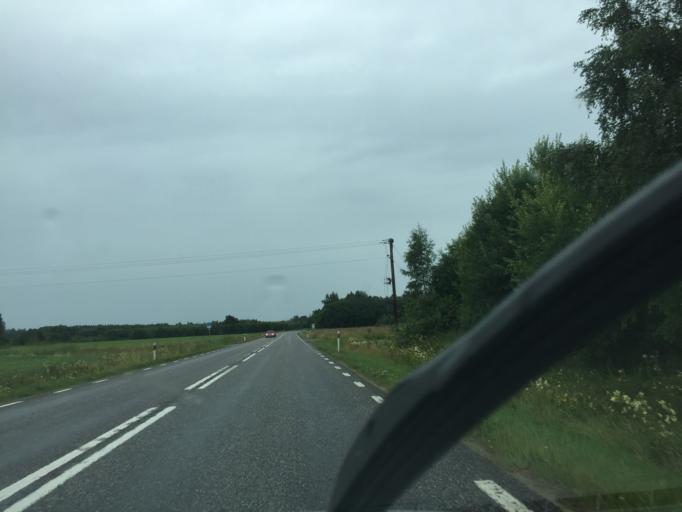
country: SE
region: OErebro
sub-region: Hallsbergs Kommun
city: Skollersta
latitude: 59.1574
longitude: 15.2658
